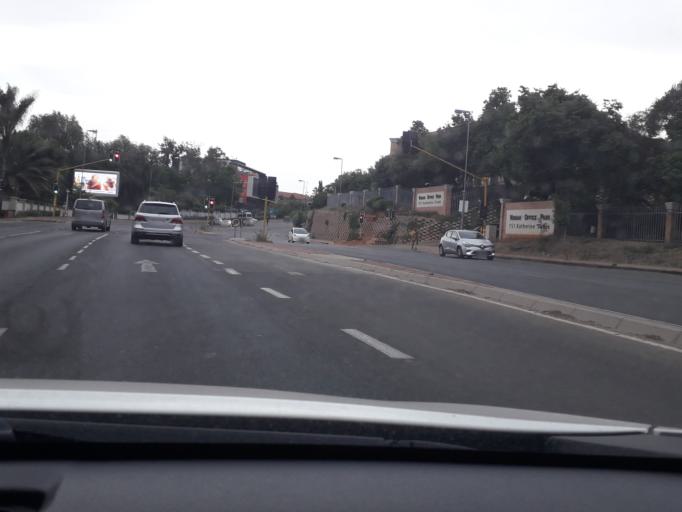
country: ZA
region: Gauteng
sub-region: City of Johannesburg Metropolitan Municipality
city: Modderfontein
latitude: -26.1010
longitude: 28.0734
